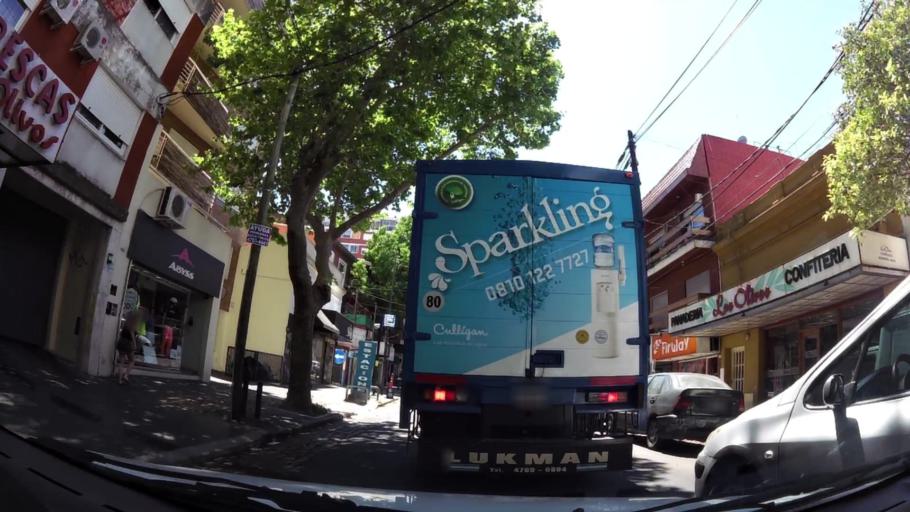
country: AR
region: Buenos Aires
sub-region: Partido de Vicente Lopez
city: Olivos
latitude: -34.5142
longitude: -58.4915
